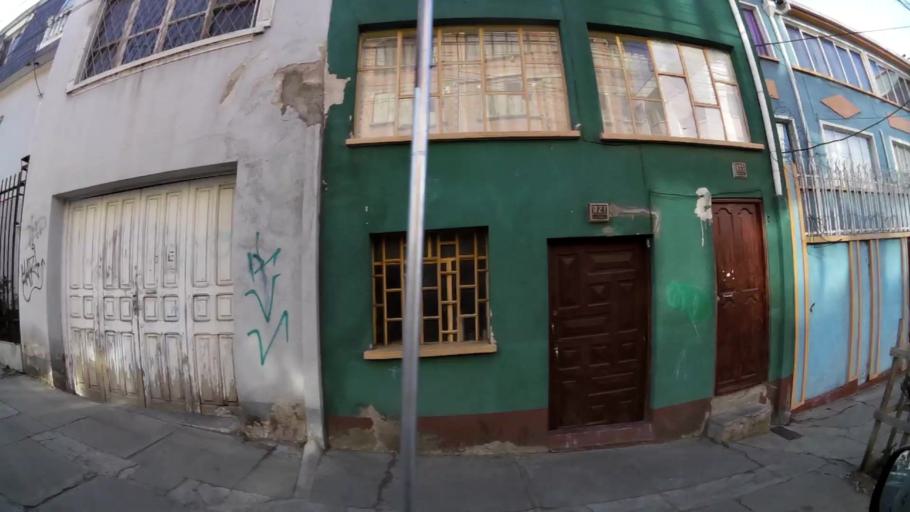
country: BO
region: La Paz
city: La Paz
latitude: -16.4877
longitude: -68.1224
